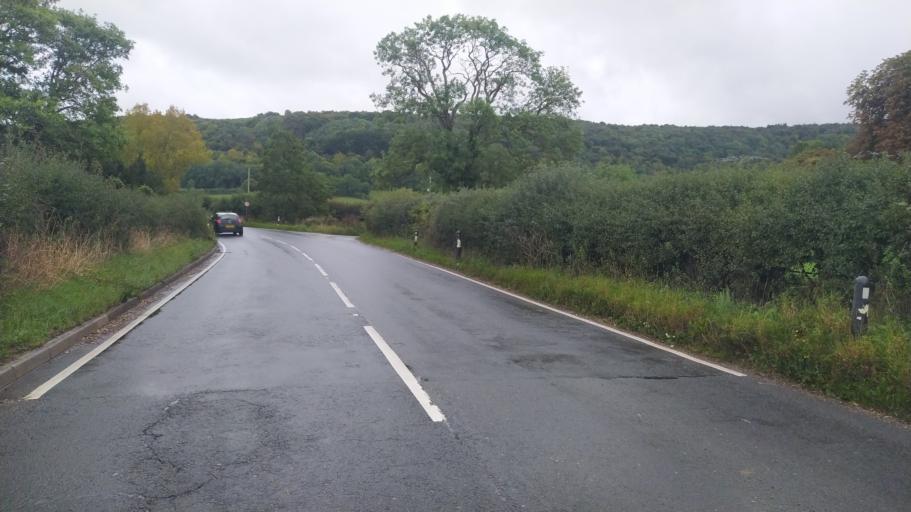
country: GB
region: England
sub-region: Dorset
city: Manston
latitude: 50.8932
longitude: -2.2388
